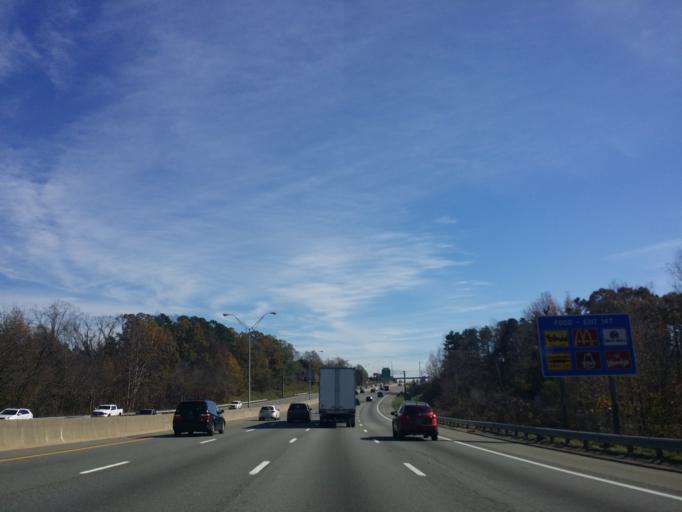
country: US
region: North Carolina
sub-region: Alamance County
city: Graham
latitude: 36.0627
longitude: -79.4163
